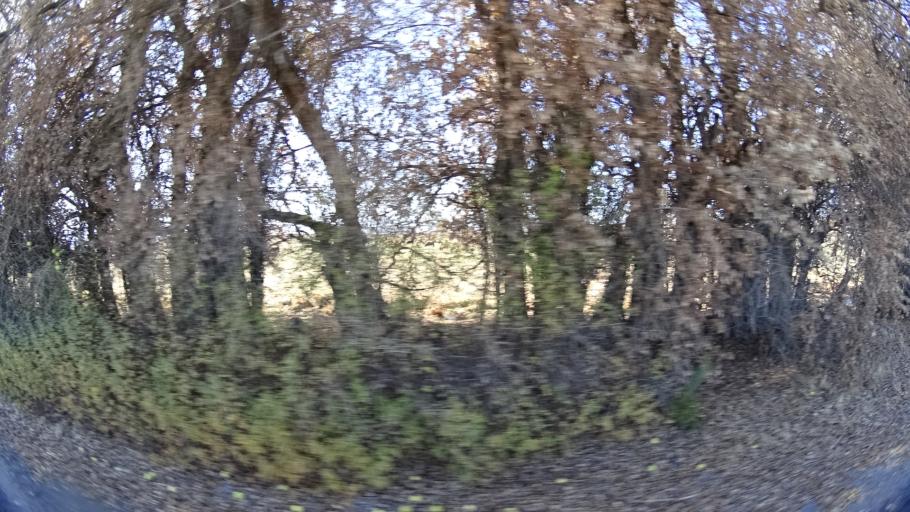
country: US
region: California
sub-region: Siskiyou County
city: Montague
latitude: 41.7223
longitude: -122.3892
